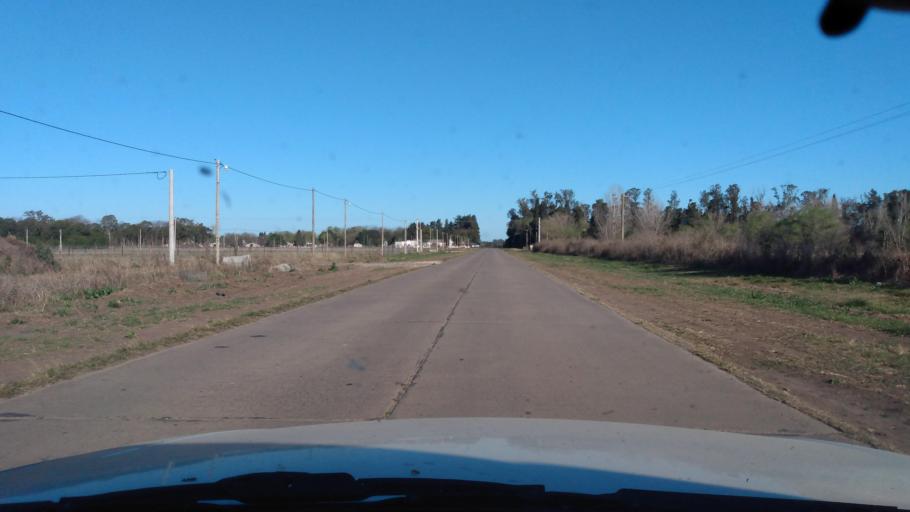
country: AR
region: Buenos Aires
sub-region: Partido de Mercedes
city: Mercedes
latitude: -34.6063
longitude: -59.2868
